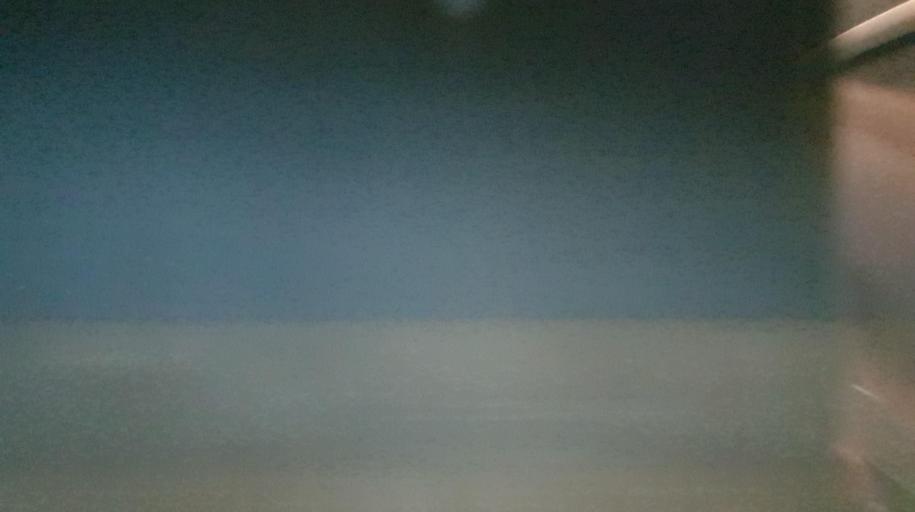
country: NO
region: Vestfold
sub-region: Sande
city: Sande
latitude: 59.5850
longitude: 10.2049
